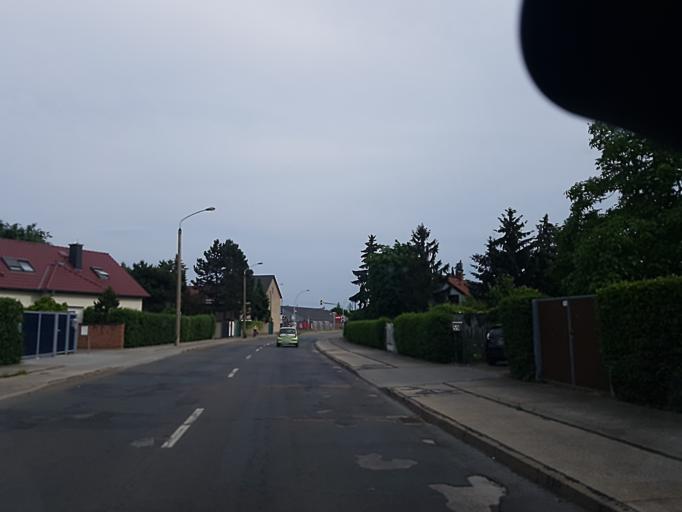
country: DE
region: Saxony-Anhalt
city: Wittenburg
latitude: 51.8767
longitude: 12.6674
